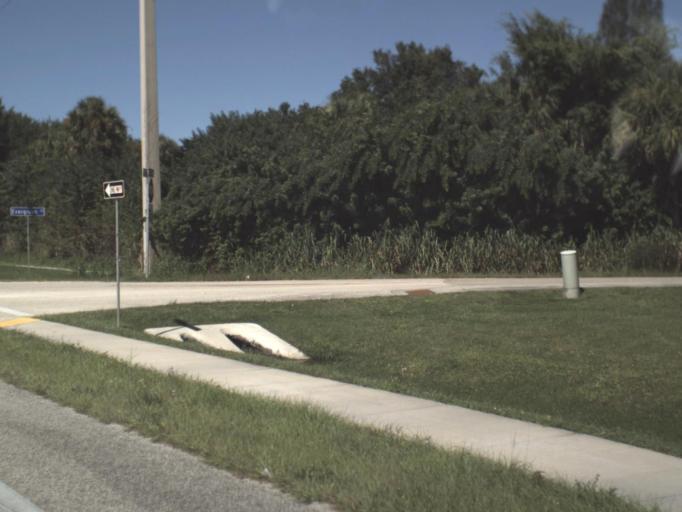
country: US
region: Florida
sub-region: Lee County
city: Palmona Park
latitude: 26.6743
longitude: -81.8961
